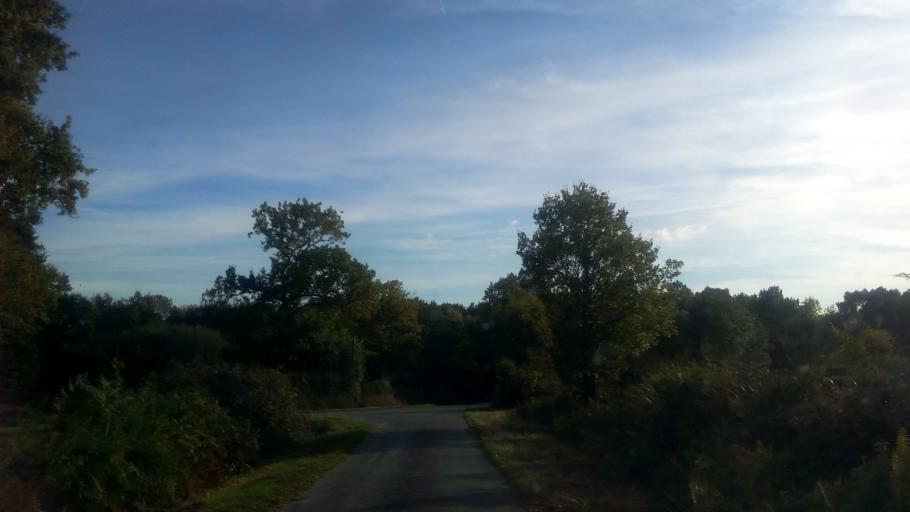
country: FR
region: Brittany
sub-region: Departement du Morbihan
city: Saint-Vincent-sur-Oust
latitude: 47.7043
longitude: -2.1122
